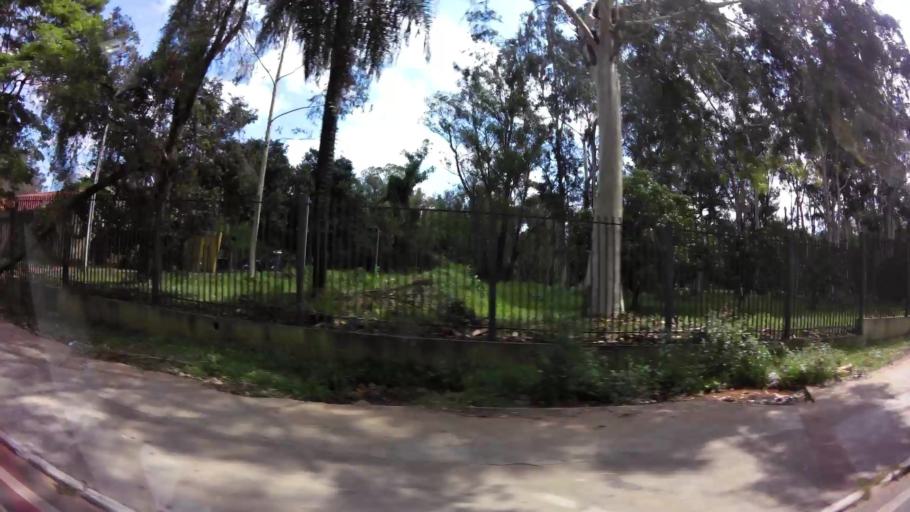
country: PY
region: Central
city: San Lorenzo
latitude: -25.3360
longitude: -57.5118
